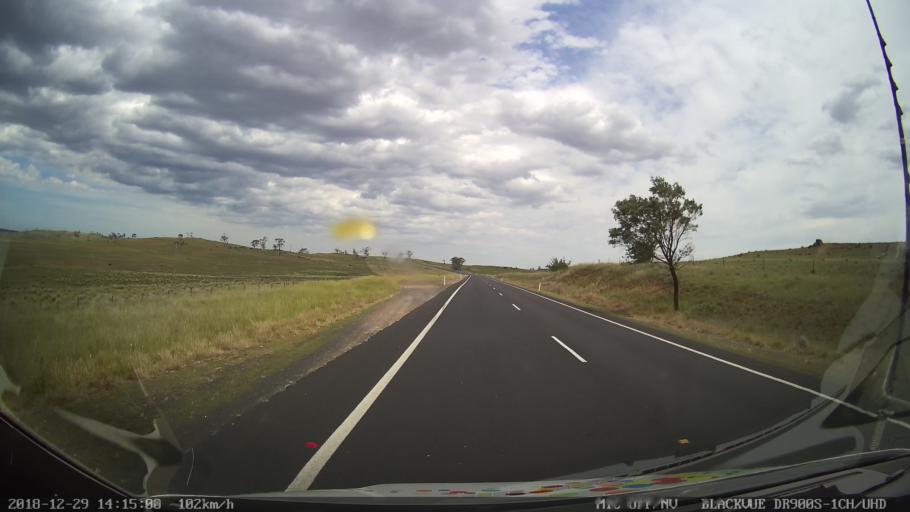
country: AU
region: New South Wales
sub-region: Cooma-Monaro
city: Cooma
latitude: -36.4501
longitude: 149.2374
